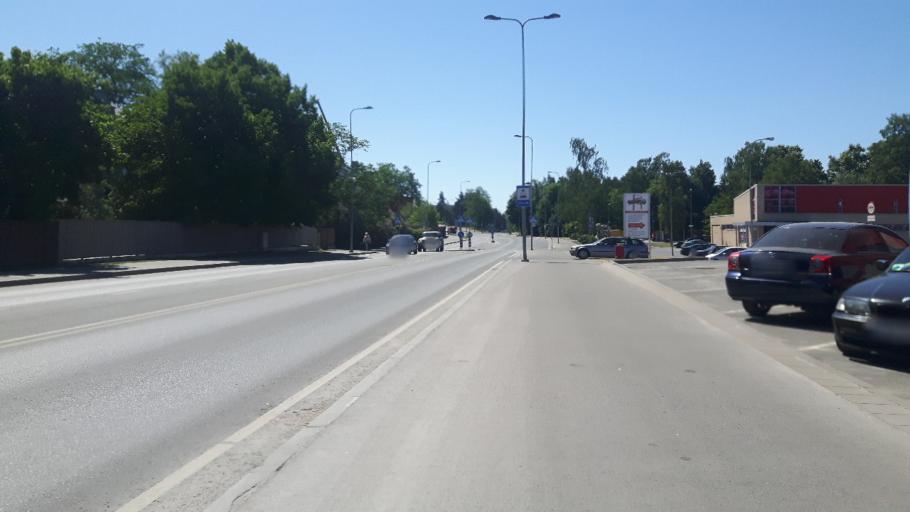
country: EE
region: Harju
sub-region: Tallinna linn
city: Tallinn
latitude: 59.3730
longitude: 24.7176
